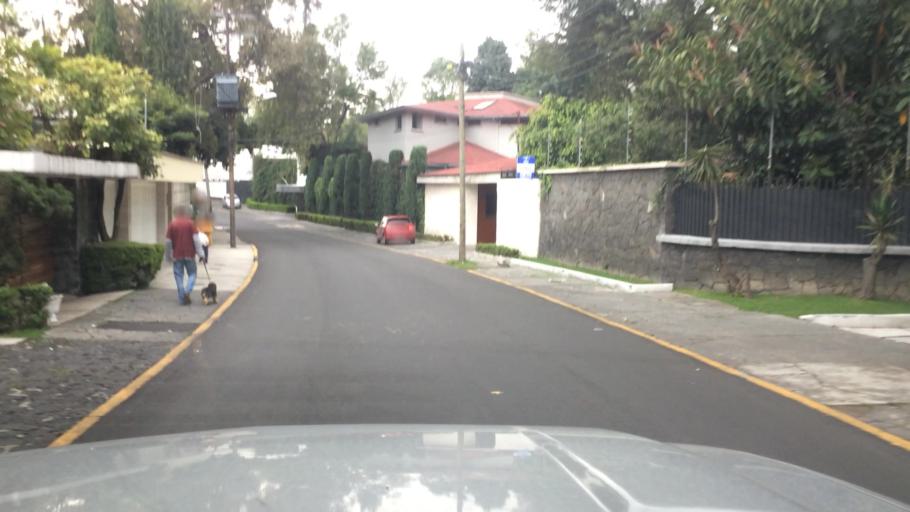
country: MX
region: Mexico City
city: Magdalena Contreras
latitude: 19.3255
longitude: -99.2089
